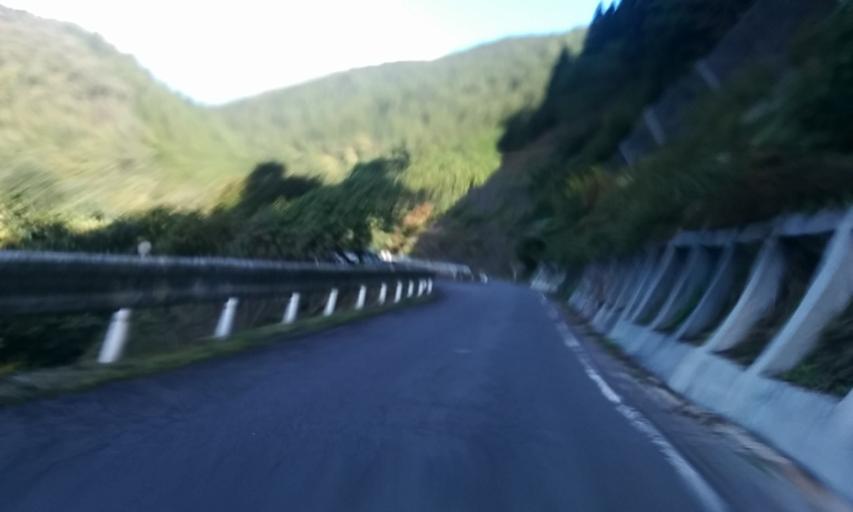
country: JP
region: Kyoto
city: Kameoka
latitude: 35.1298
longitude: 135.5602
